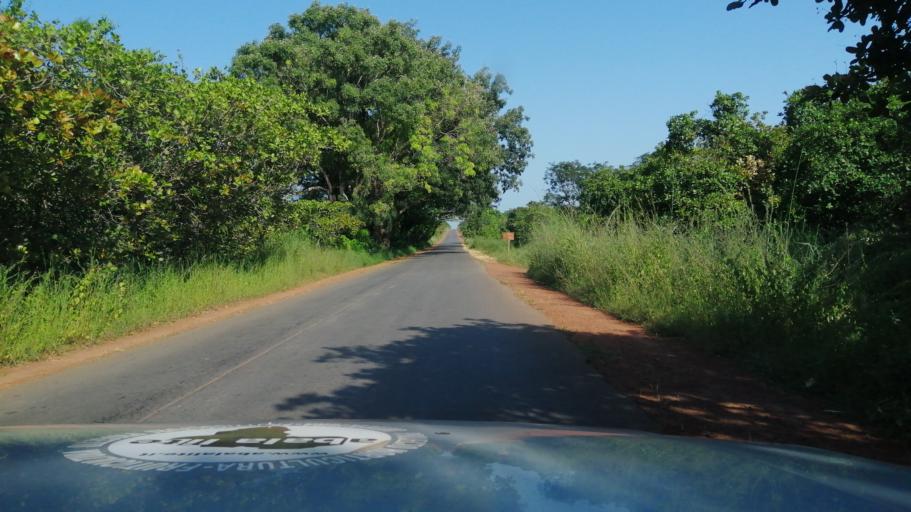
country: GW
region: Bissau
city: Bissau
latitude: 11.9588
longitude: -15.5296
